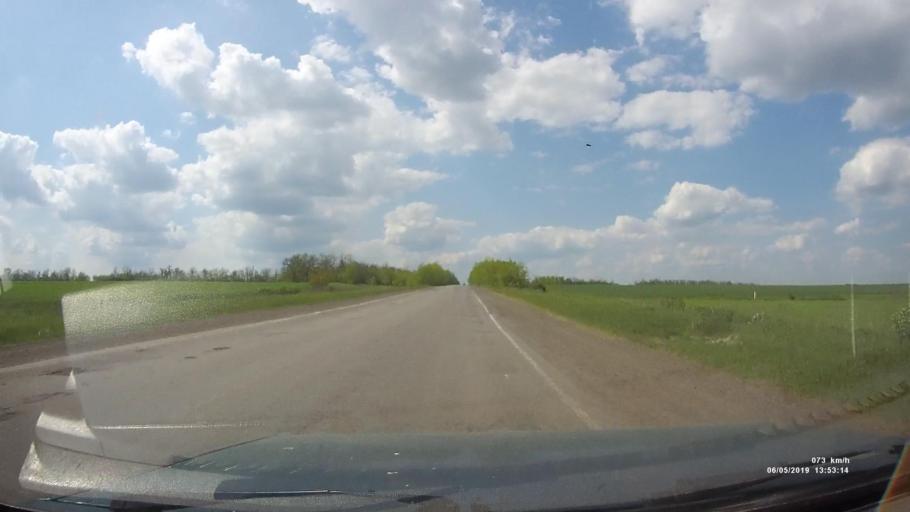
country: RU
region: Rostov
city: Melikhovskaya
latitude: 47.6671
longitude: 40.4651
